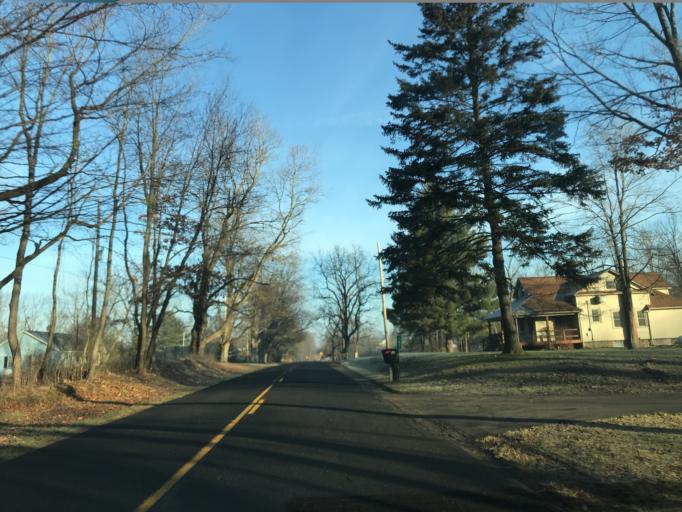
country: US
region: Michigan
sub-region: Ingham County
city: Holt
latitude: 42.5785
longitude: -84.5822
